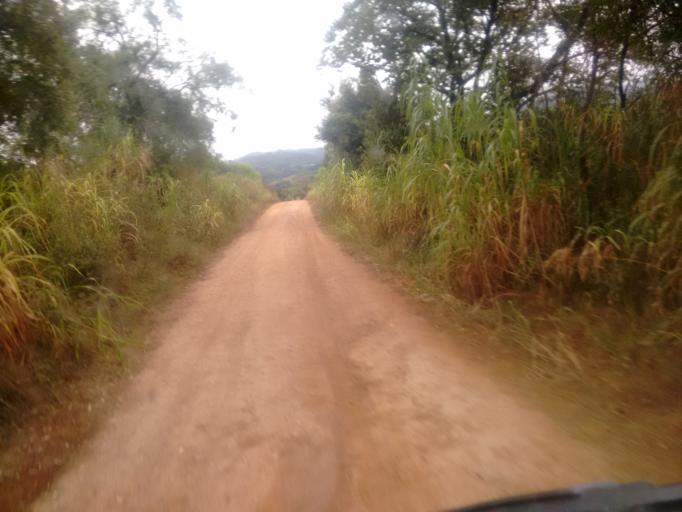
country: BR
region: Rio Grande do Sul
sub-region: Camaqua
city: Camaqua
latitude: -30.7239
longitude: -51.8585
